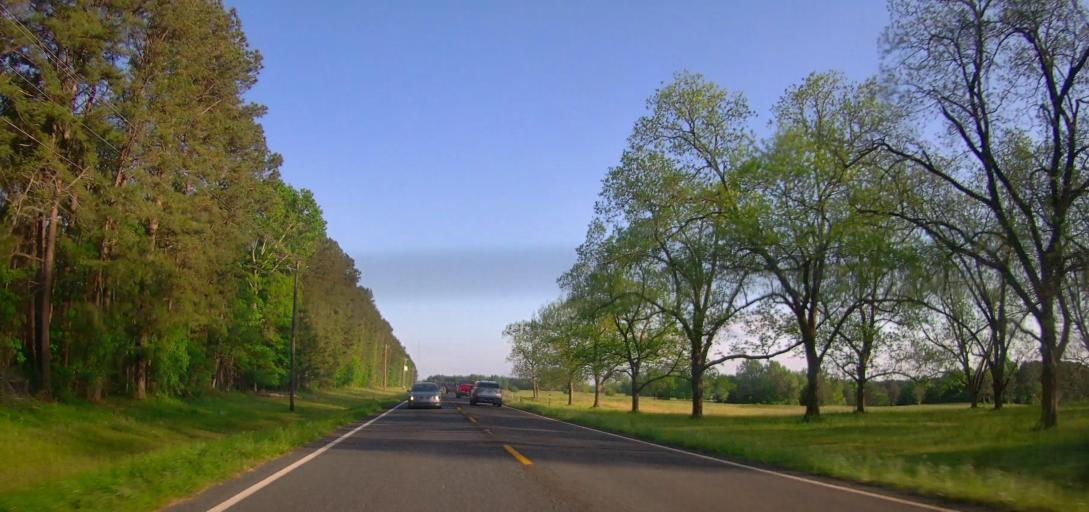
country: US
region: Georgia
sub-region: Jasper County
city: Monticello
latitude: 33.4556
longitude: -83.6311
